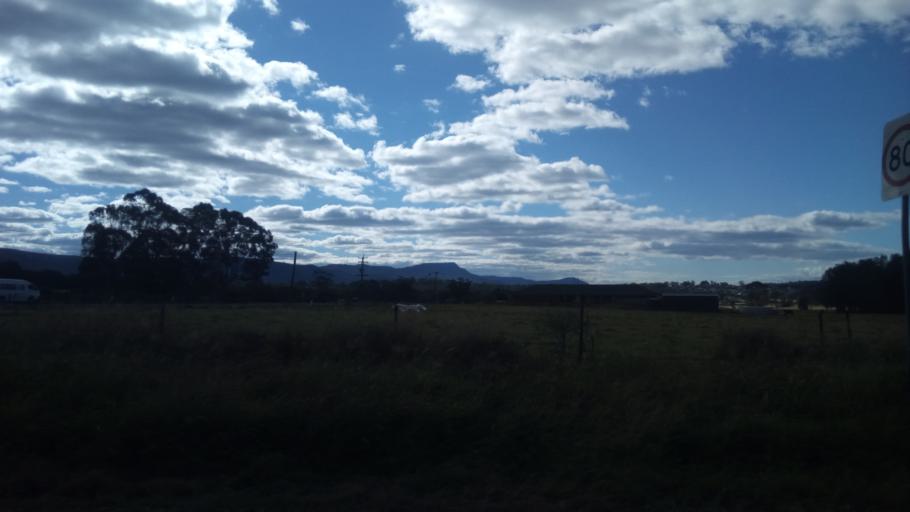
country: AU
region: New South Wales
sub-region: Shellharbour
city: Albion Park Rail
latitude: -34.5361
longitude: 150.7684
